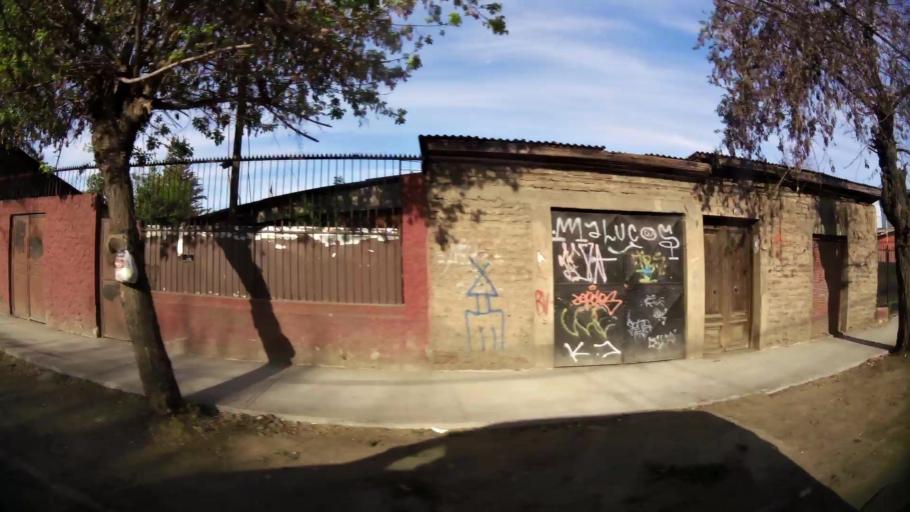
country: CL
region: Santiago Metropolitan
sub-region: Provincia de Santiago
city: Lo Prado
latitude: -33.4449
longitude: -70.7073
